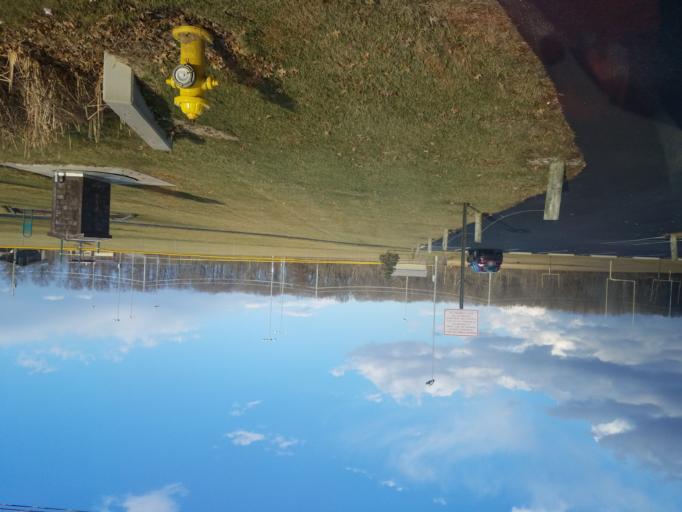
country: US
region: Ohio
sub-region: Delaware County
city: Delaware
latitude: 40.3244
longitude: -83.0979
